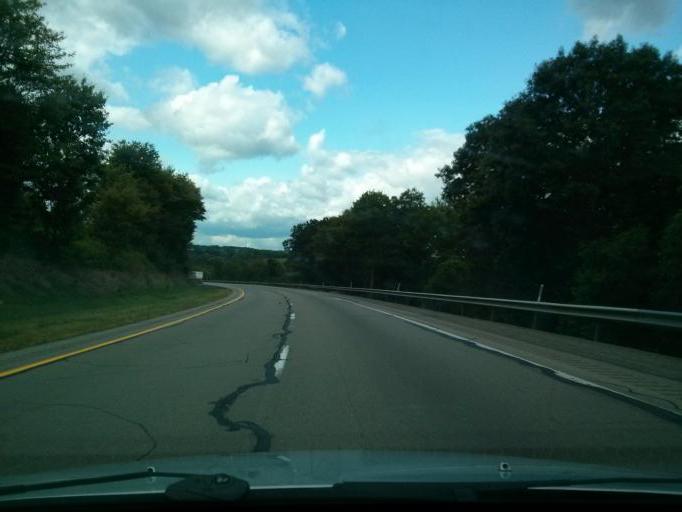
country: US
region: Pennsylvania
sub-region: Jefferson County
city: Brookville
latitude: 41.1707
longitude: -79.0162
